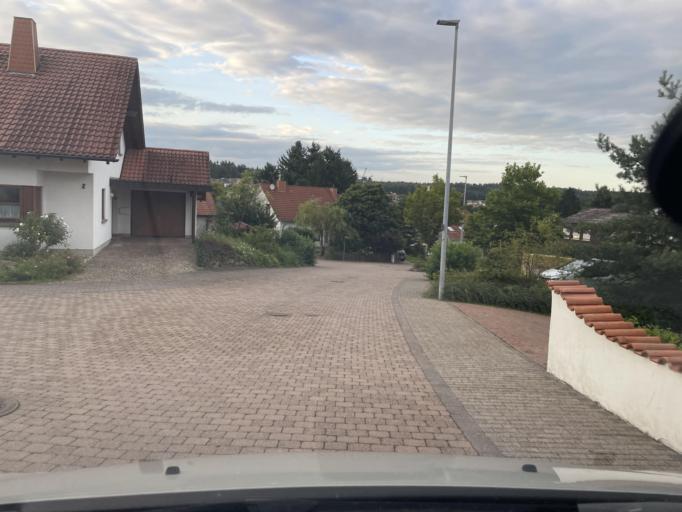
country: DE
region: Saarland
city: Sankt Ingbert
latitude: 49.2835
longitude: 7.1298
